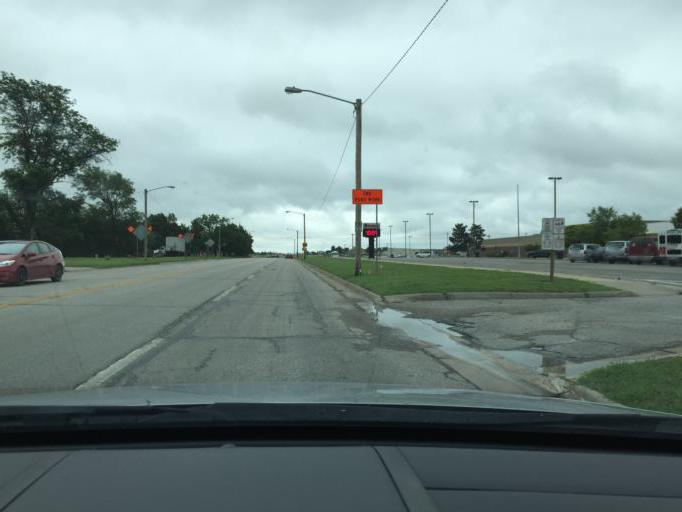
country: US
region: Kansas
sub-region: McPherson County
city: Moundridge
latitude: 38.2030
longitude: -97.5127
